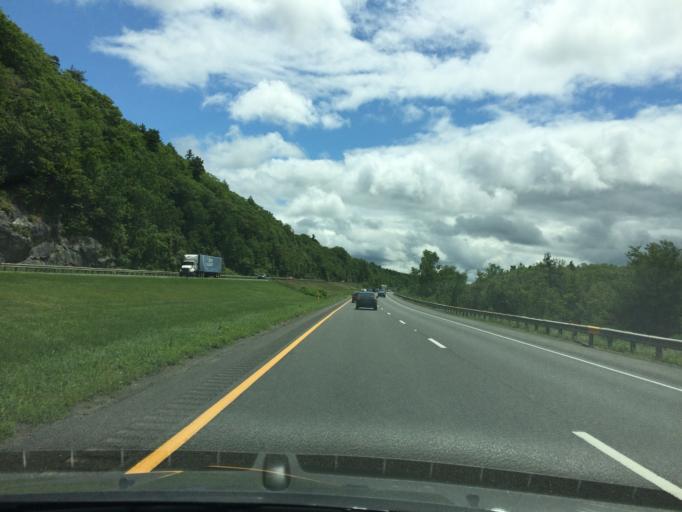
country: US
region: Massachusetts
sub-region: Berkshire County
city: Becket
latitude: 42.2757
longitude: -73.1397
